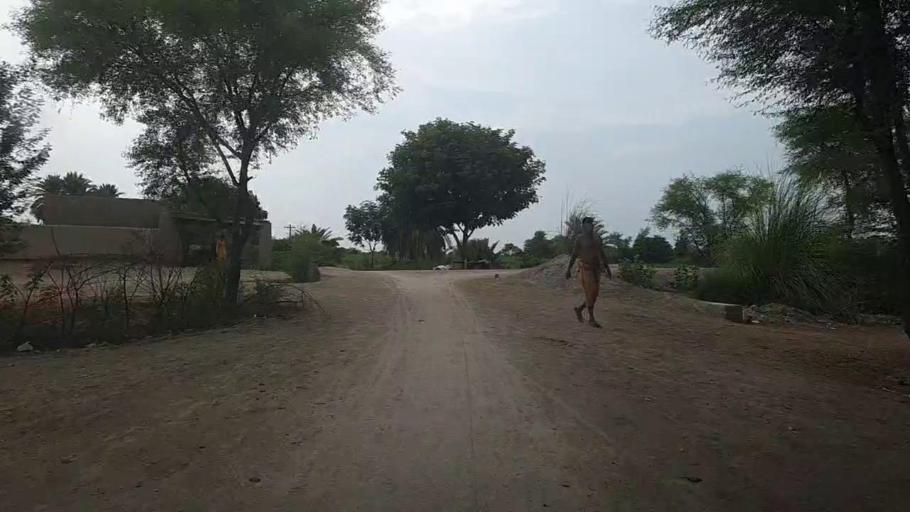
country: PK
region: Sindh
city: Karaundi
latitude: 26.9679
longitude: 68.4246
